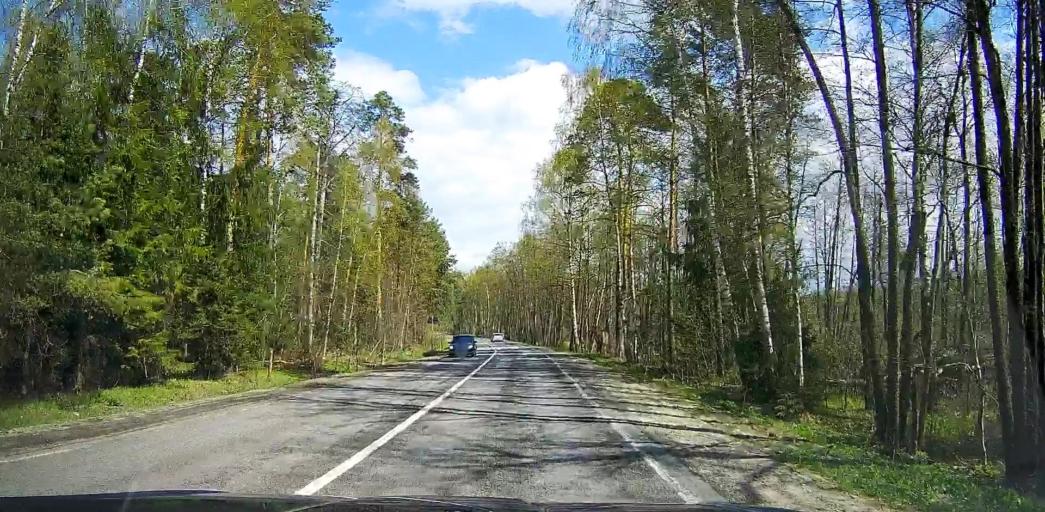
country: RU
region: Moskovskaya
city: Davydovo
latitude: 55.5620
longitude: 38.8527
